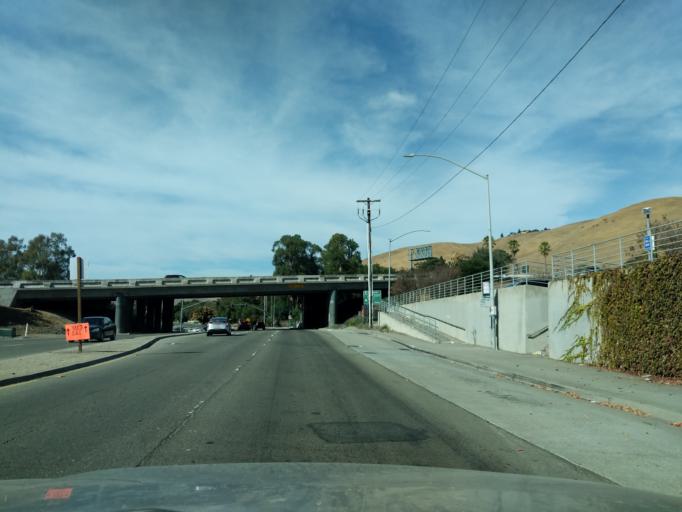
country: US
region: California
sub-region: Alameda County
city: Fremont
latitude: 37.5399
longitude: -121.9239
